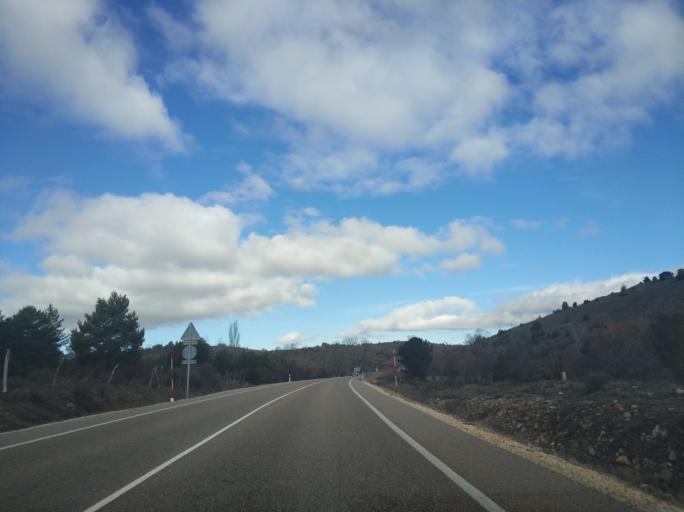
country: ES
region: Castille and Leon
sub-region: Provincia de Burgos
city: Rabanera del Pinar
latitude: 41.8789
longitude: -3.2240
